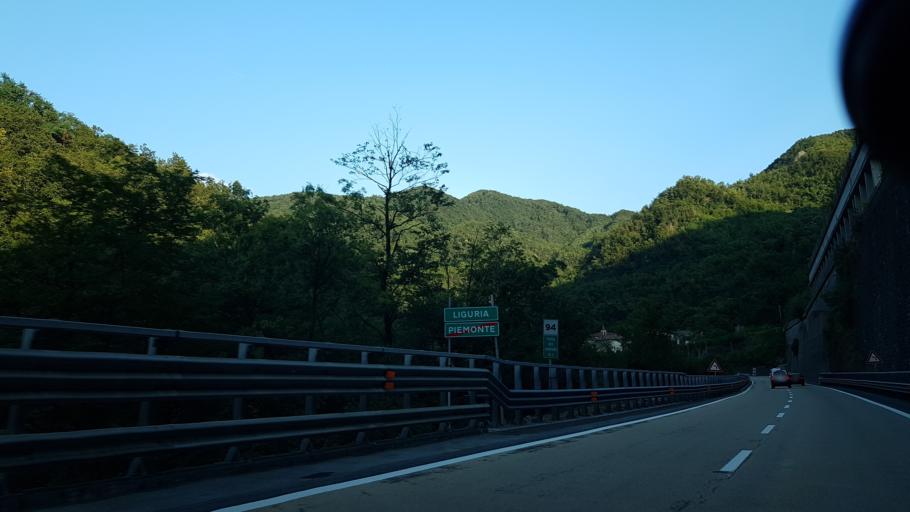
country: IT
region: Piedmont
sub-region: Provincia di Alessandria
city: Arquata Scrivia
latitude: 44.6607
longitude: 8.9176
